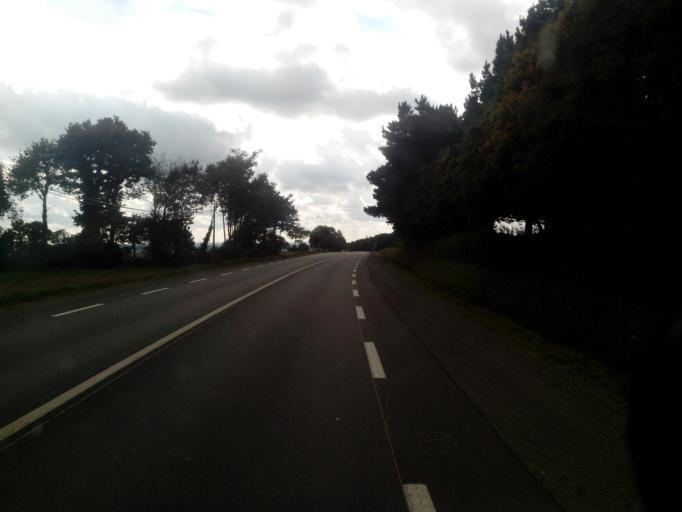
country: FR
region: Brittany
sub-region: Departement du Morbihan
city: Mauron
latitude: 48.0295
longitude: -2.3087
